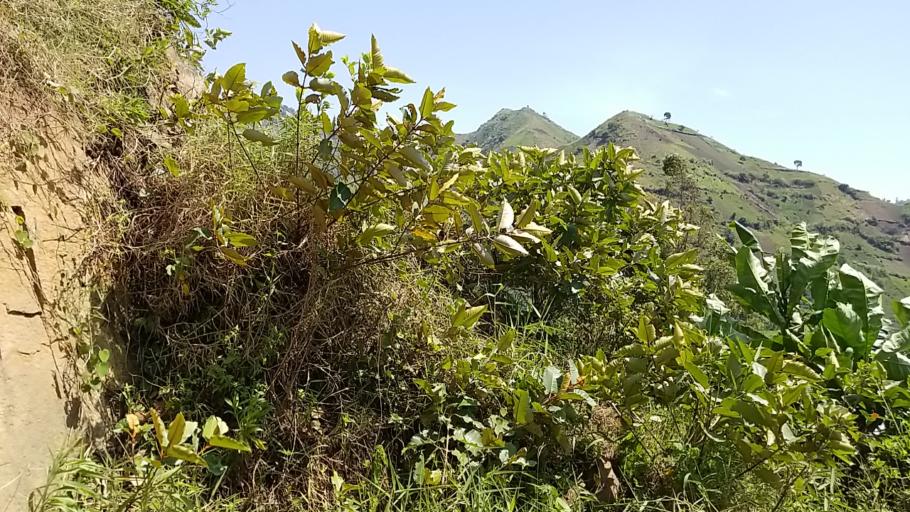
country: CD
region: Nord Kivu
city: Sake
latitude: -1.7724
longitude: 29.0051
